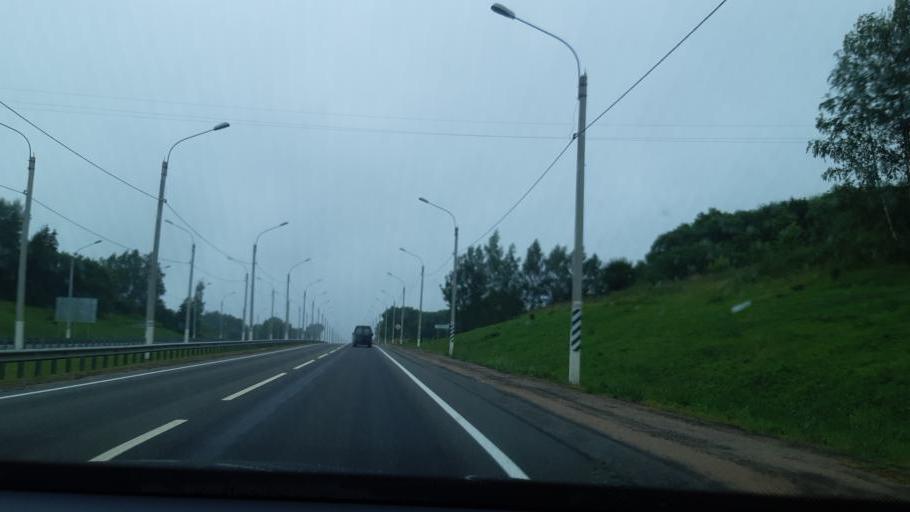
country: RU
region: Smolensk
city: Talashkino
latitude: 54.6376
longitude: 32.1801
